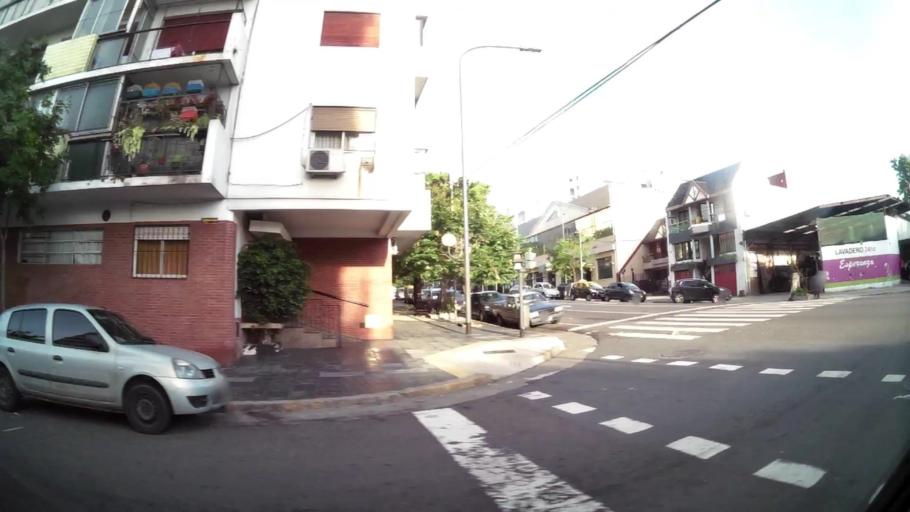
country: AR
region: Buenos Aires F.D.
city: Buenos Aires
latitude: -34.6325
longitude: -58.4270
